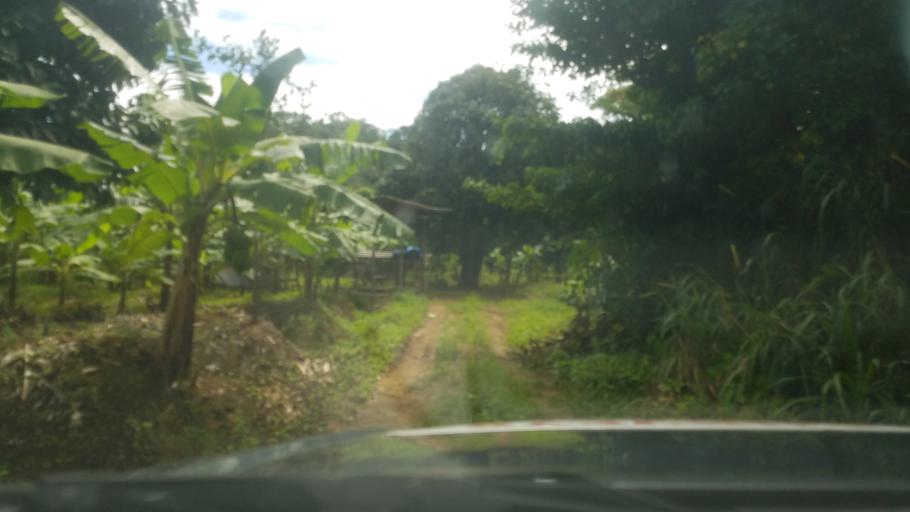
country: LC
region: Dennery Quarter
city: Dennery
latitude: 13.9329
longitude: -60.9201
